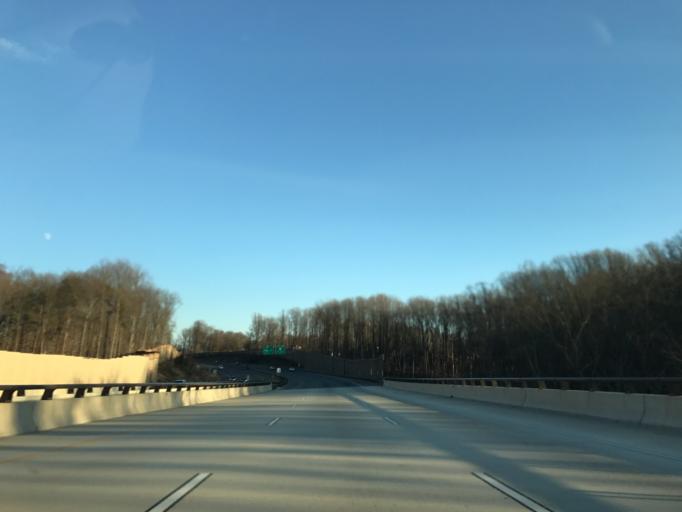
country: US
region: Maryland
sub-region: Montgomery County
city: Fairland
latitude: 39.0841
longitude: -76.9719
